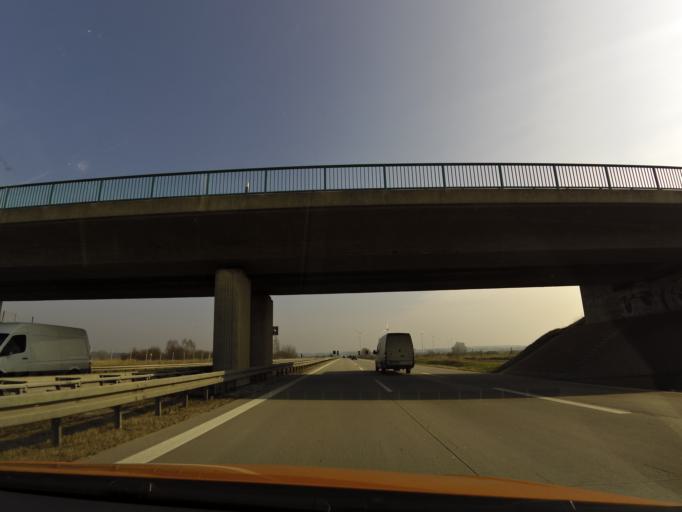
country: DE
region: Brandenburg
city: Jacobsdorf
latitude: 52.3220
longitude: 14.3512
